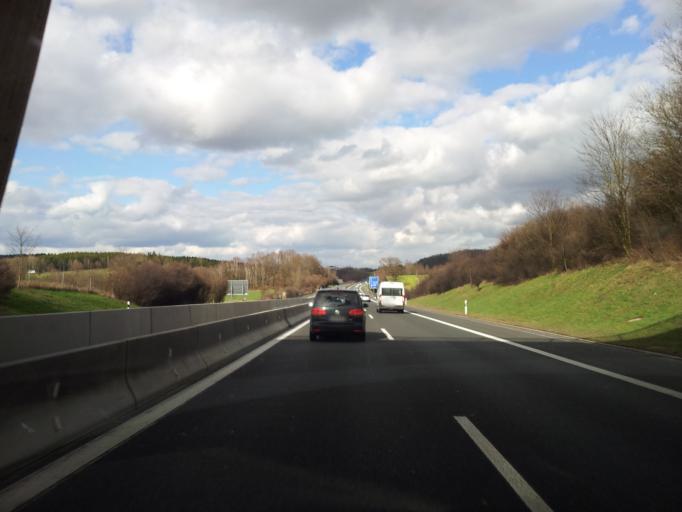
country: DE
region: Saxony
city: Neuensalz
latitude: 50.4927
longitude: 12.1916
